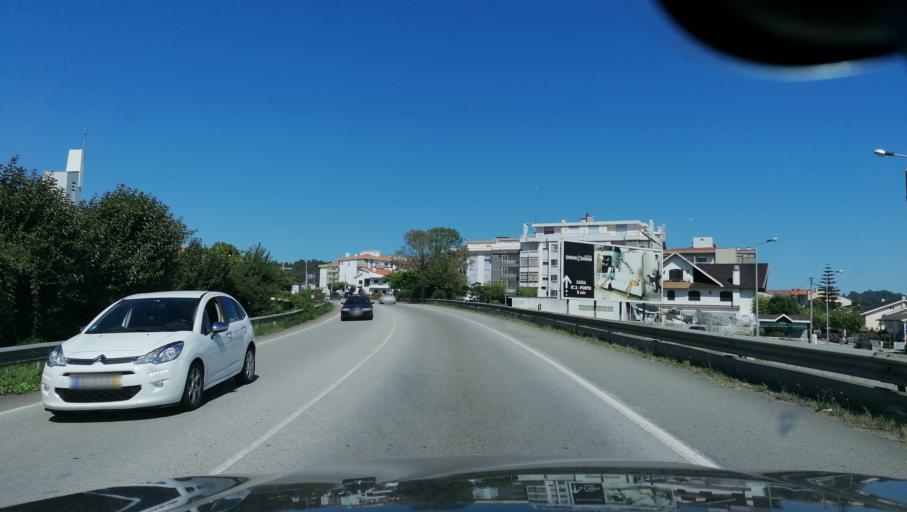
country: PT
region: Aveiro
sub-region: Santa Maria da Feira
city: Feira
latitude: 40.9262
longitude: -8.5596
